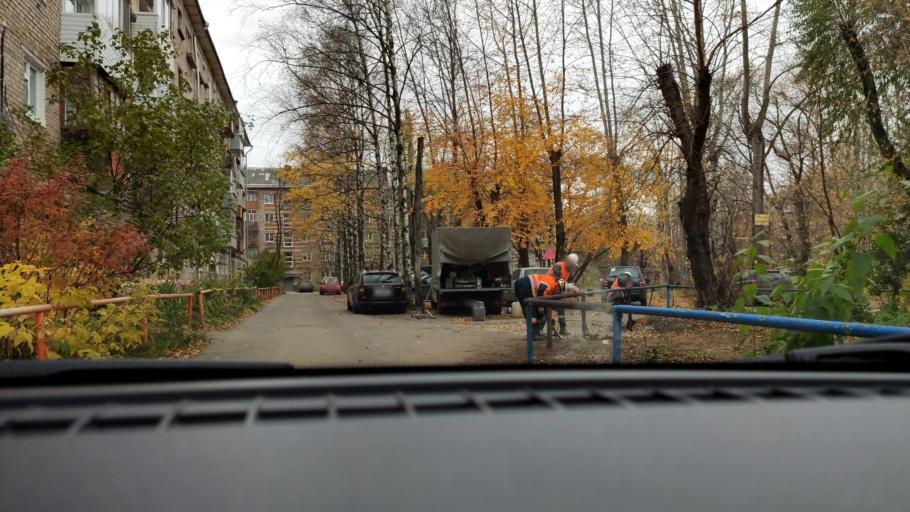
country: RU
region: Perm
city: Perm
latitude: 57.9971
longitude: 56.2934
